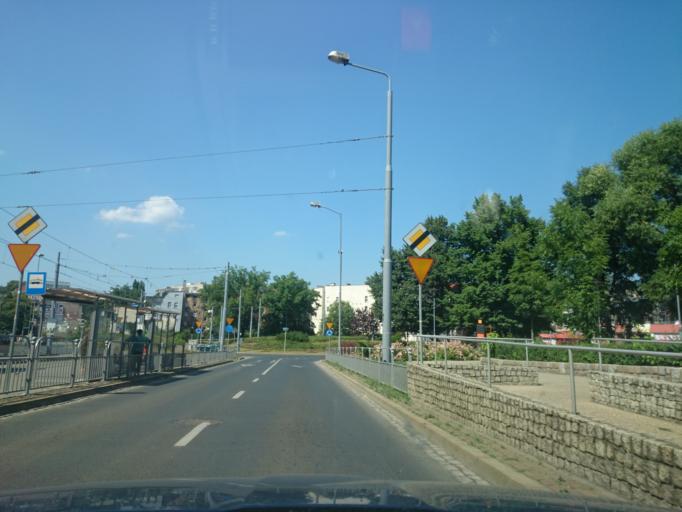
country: PL
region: West Pomeranian Voivodeship
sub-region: Szczecin
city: Szczecin
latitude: 53.4426
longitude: 14.5478
